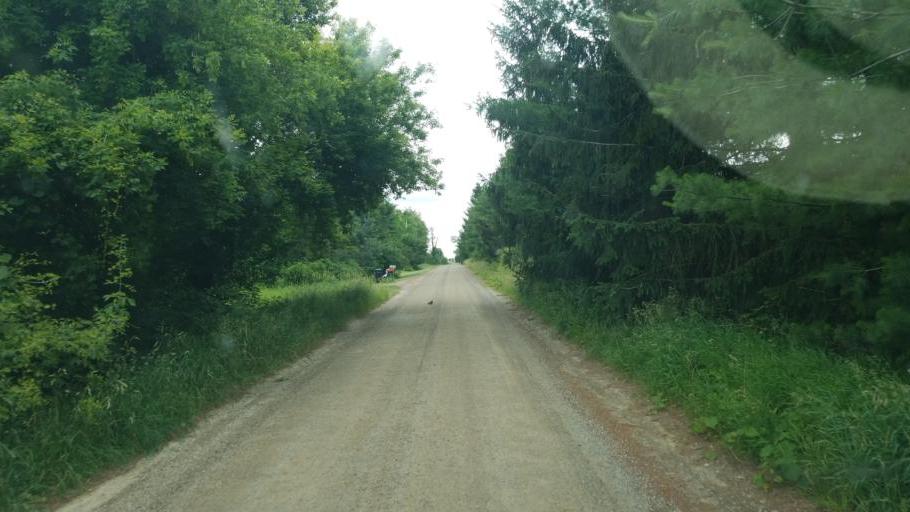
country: US
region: Michigan
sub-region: Barry County
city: Nashville
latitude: 42.6898
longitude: -84.9756
